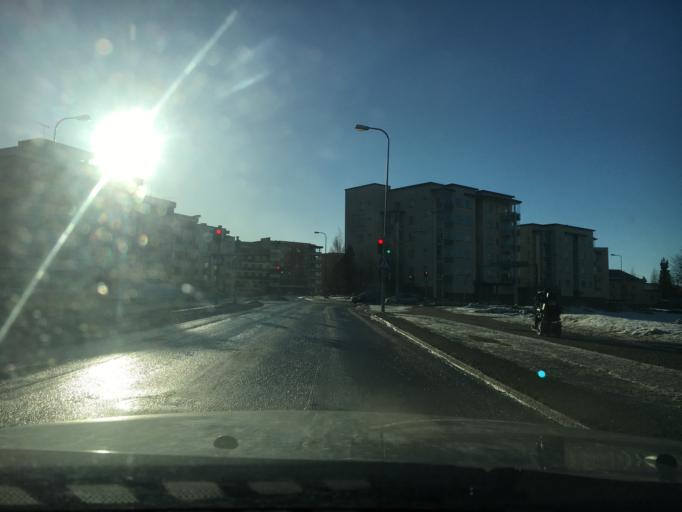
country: FI
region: Kainuu
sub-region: Kajaani
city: Kajaani
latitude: 64.2216
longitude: 27.7420
